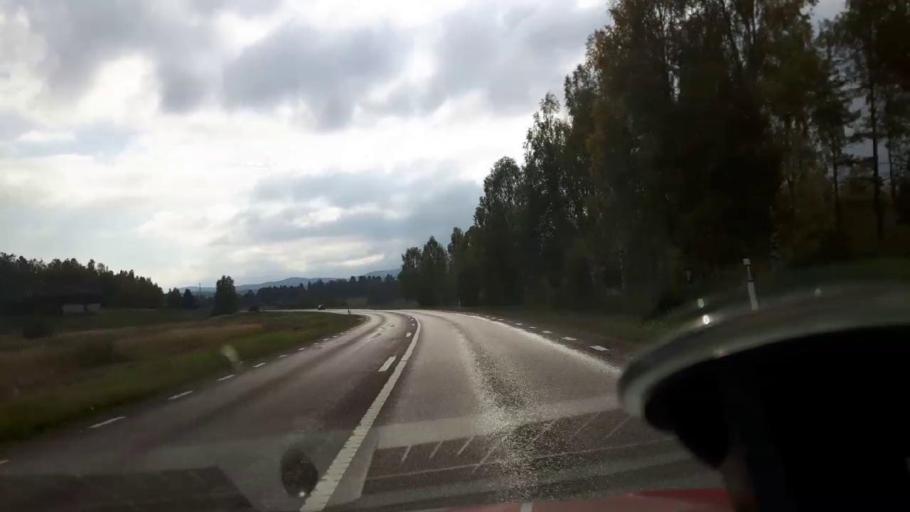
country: SE
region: Gaevleborg
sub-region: Bollnas Kommun
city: Kilafors
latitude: 61.2404
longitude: 16.5507
